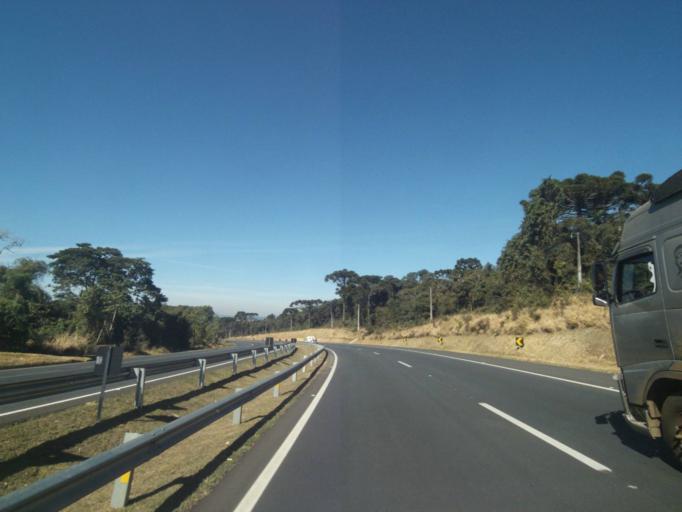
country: BR
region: Parana
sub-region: Carambei
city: Carambei
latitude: -24.9066
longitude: -50.4223
